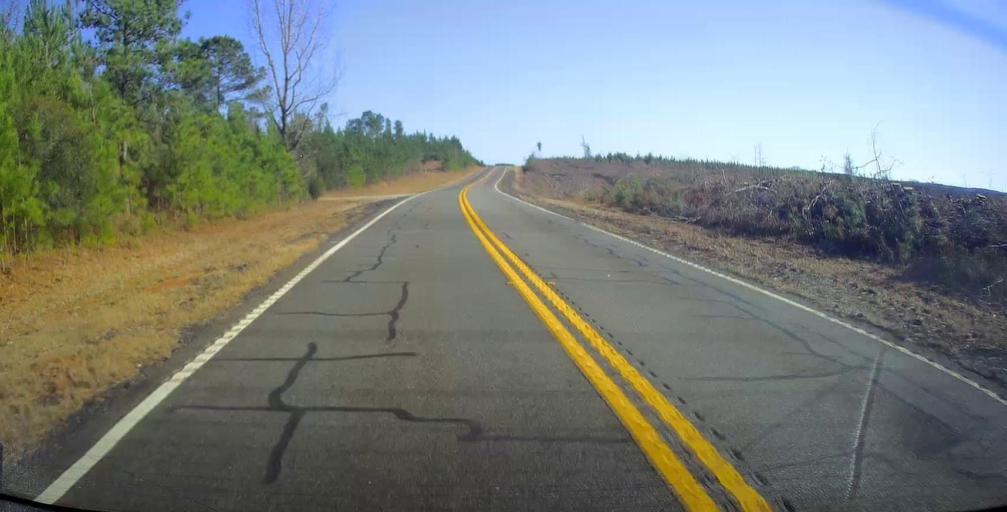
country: US
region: Georgia
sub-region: Talbot County
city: Talbotton
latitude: 32.6625
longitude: -84.4612
